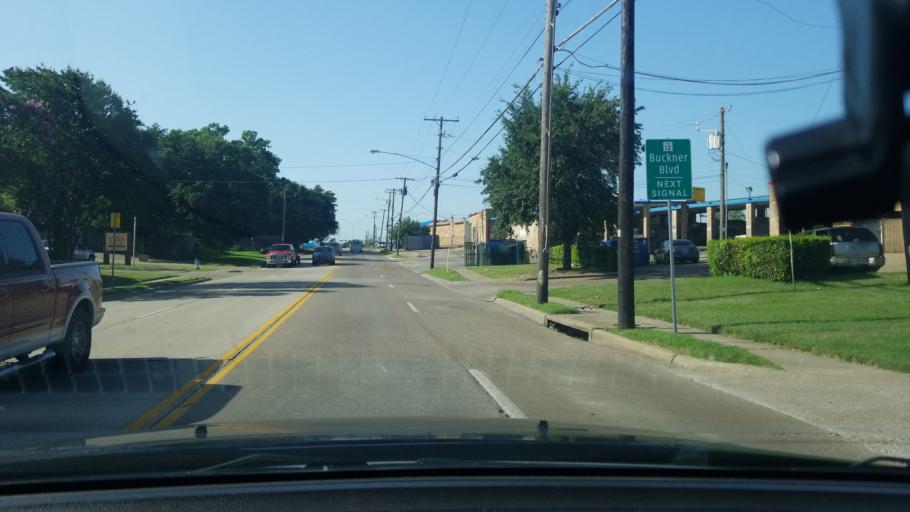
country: US
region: Texas
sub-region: Dallas County
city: Mesquite
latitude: 32.8113
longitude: -96.6841
